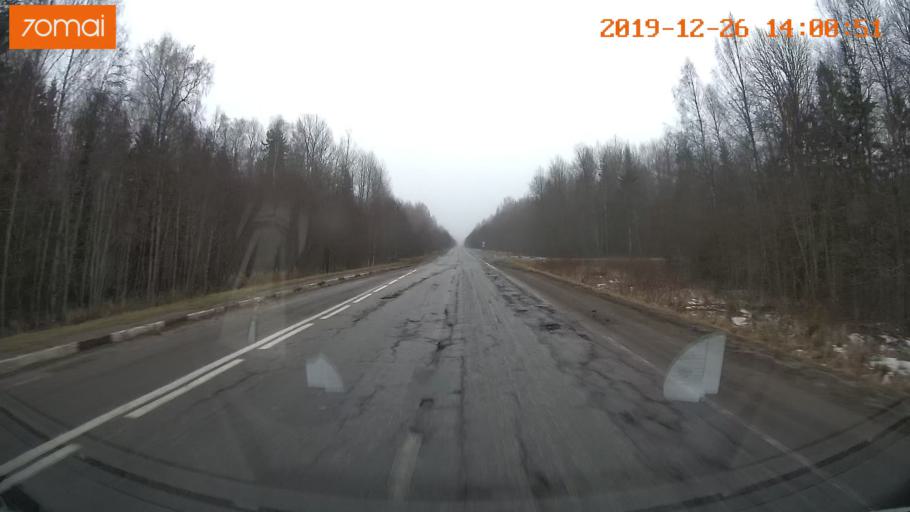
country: RU
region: Jaroslavl
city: Poshekhon'ye
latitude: 58.5550
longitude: 38.7518
